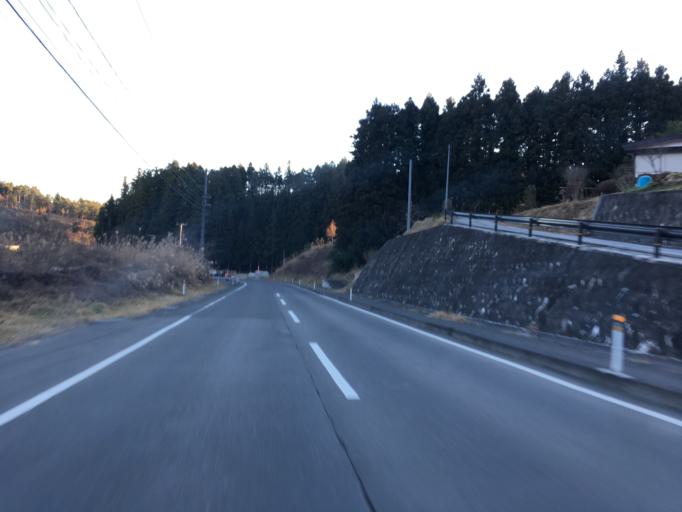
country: JP
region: Fukushima
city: Ishikawa
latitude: 37.1911
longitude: 140.5615
